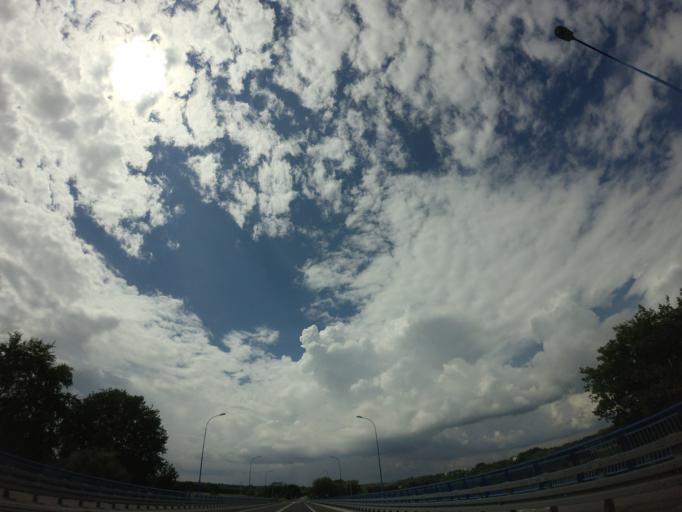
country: PL
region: Masovian Voivodeship
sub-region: Powiat lipski
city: Solec Nad Wisla
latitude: 51.1251
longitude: 21.7890
